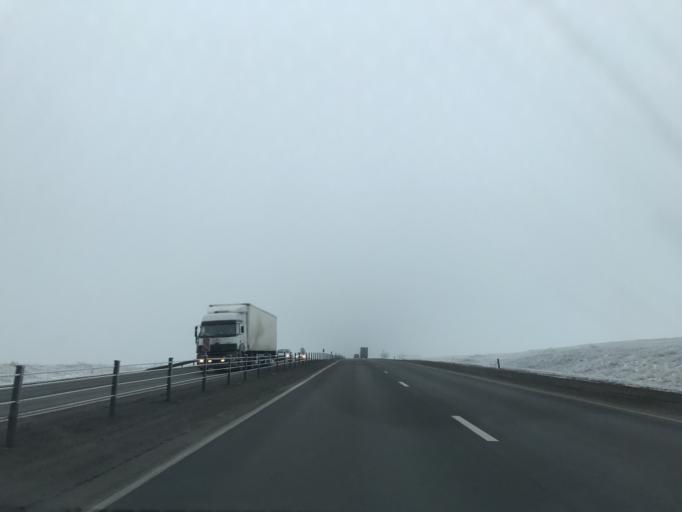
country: RU
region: Rostov
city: Likhoy
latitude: 48.1489
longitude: 40.2607
